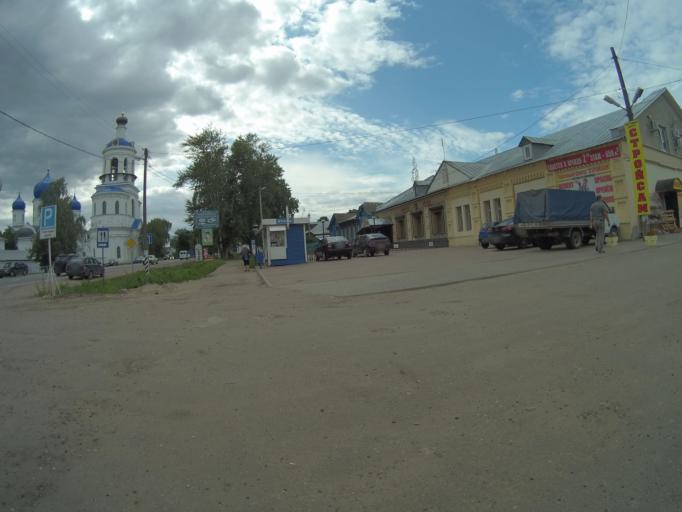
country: RU
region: Vladimir
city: Bogolyubovo
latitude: 56.1976
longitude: 40.5379
